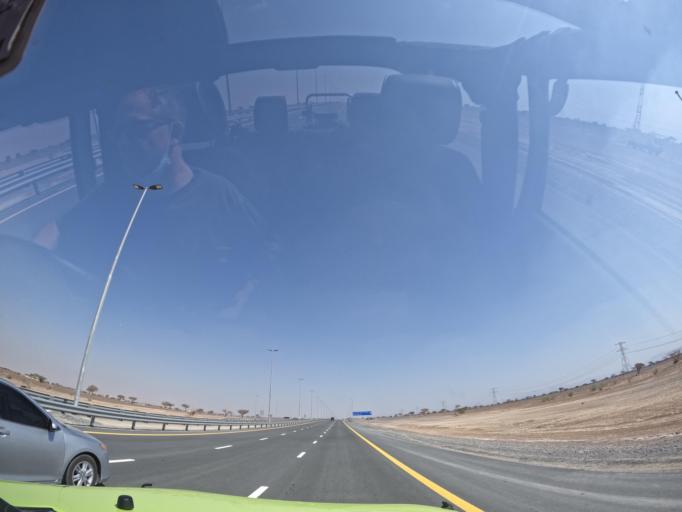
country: AE
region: Ash Shariqah
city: Adh Dhayd
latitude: 24.9503
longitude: 55.8341
